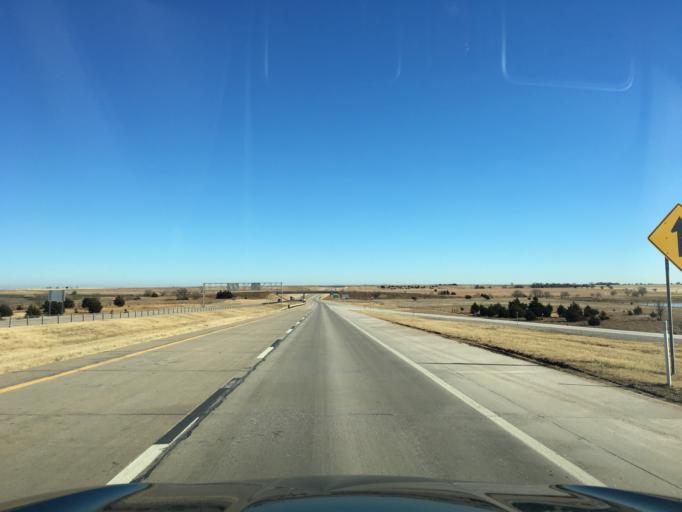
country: US
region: Oklahoma
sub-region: Noble County
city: Perry
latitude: 36.4001
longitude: -97.3245
